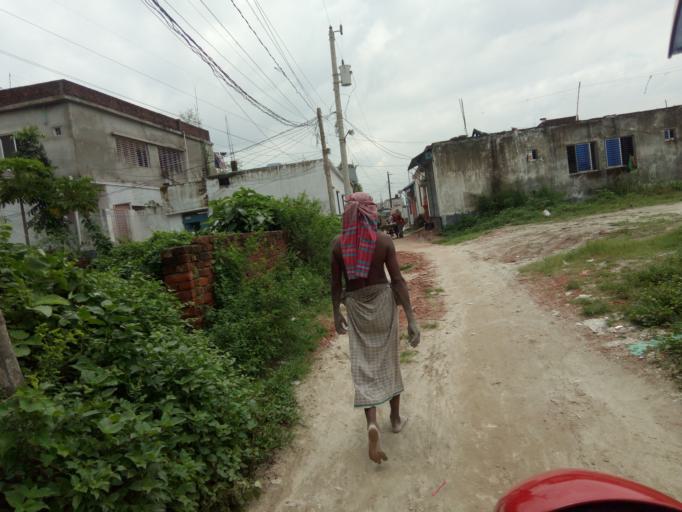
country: BD
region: Dhaka
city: Azimpur
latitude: 23.7356
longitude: 90.3449
